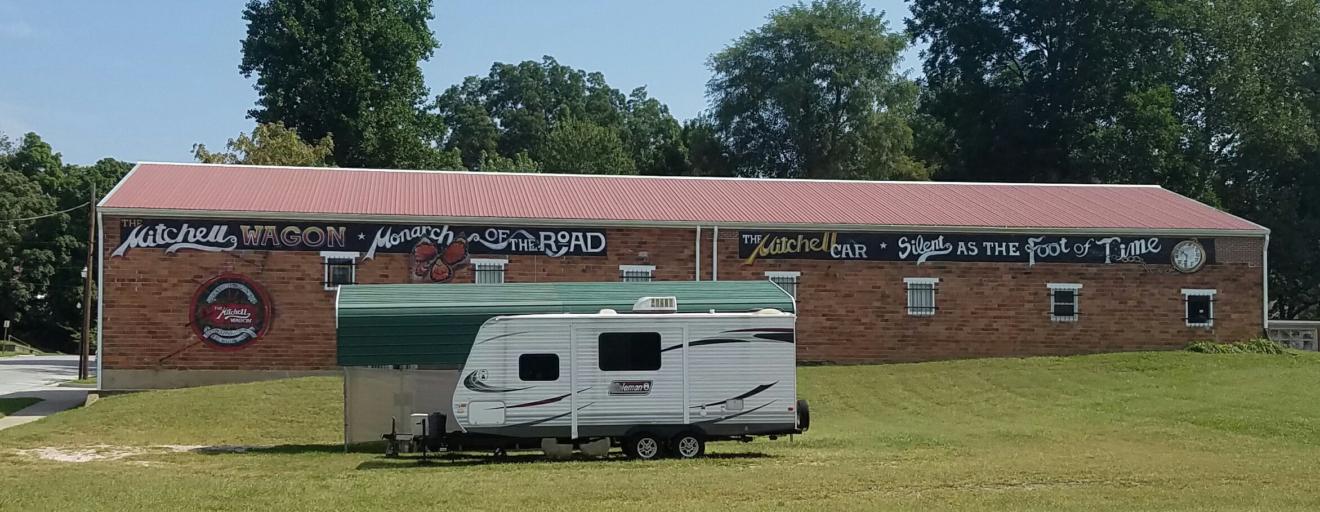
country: US
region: Missouri
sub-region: Cooper County
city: Boonville
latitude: 38.9764
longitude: -92.7489
